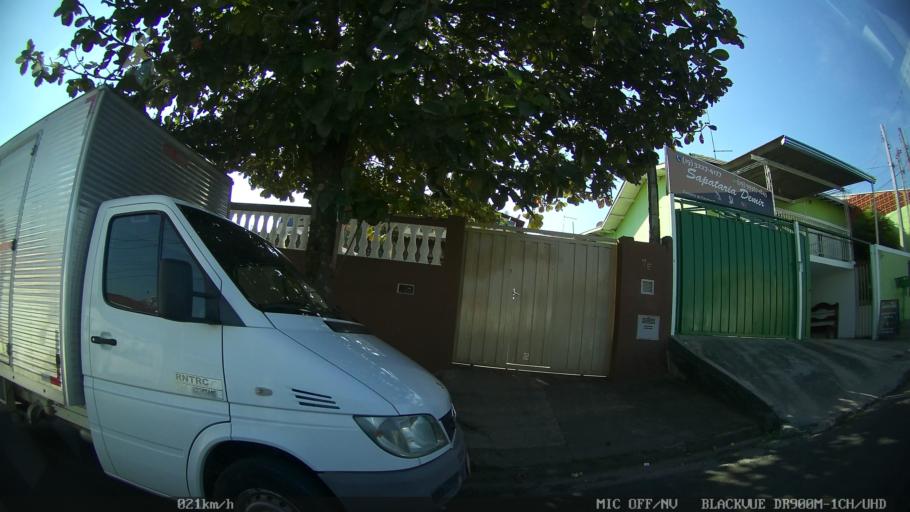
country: BR
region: Sao Paulo
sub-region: Campinas
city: Campinas
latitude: -22.9569
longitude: -47.0910
